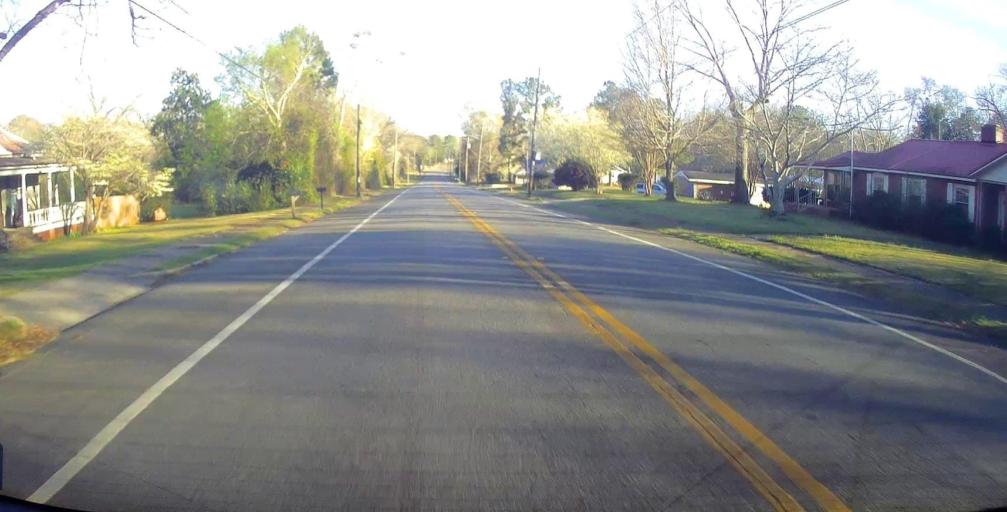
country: US
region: Georgia
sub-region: Talbot County
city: Talbotton
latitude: 32.6715
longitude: -84.5370
